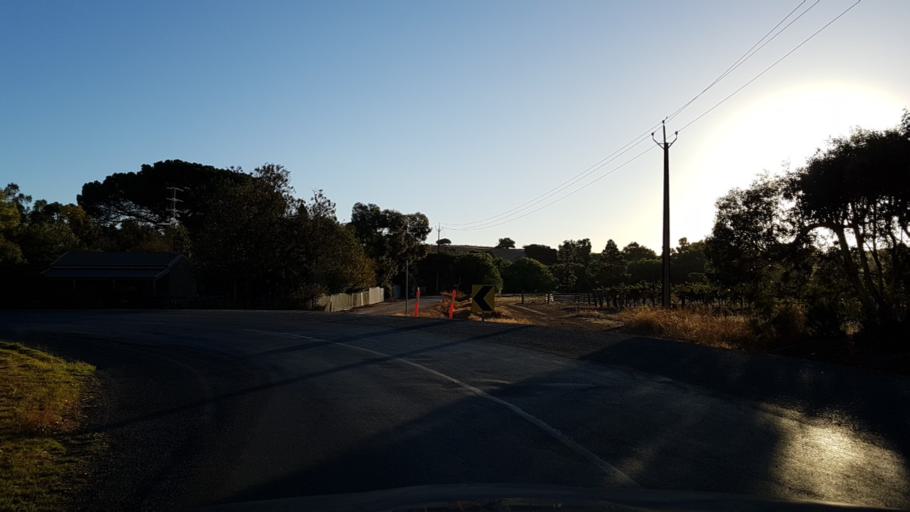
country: AU
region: South Australia
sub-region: Clare and Gilbert Valleys
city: Clare
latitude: -34.0229
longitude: 138.6884
